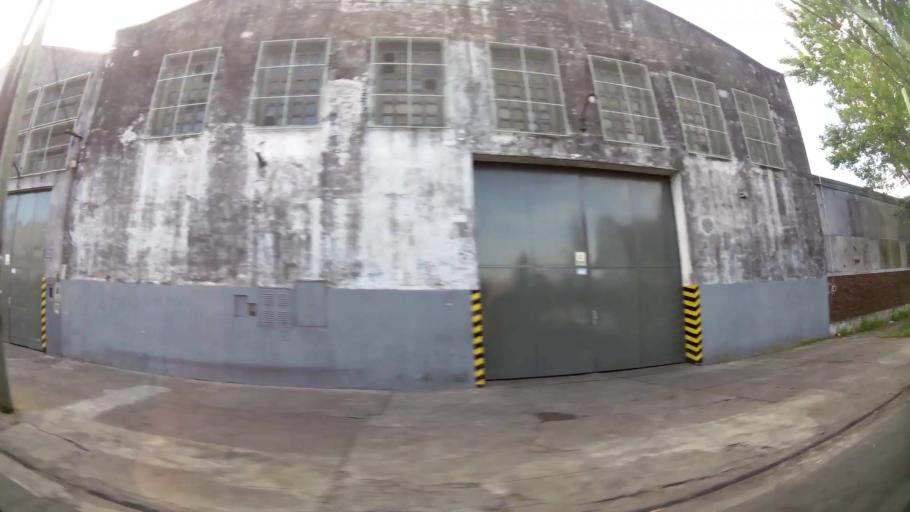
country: AR
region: Buenos Aires
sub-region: Partido de Avellaneda
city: Avellaneda
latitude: -34.6806
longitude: -58.3566
